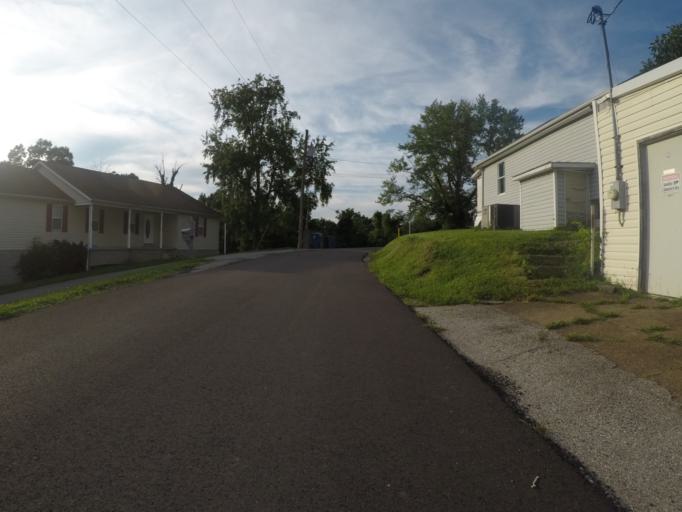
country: US
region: West Virginia
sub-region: Cabell County
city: Pea Ridge
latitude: 38.4064
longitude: -82.3631
